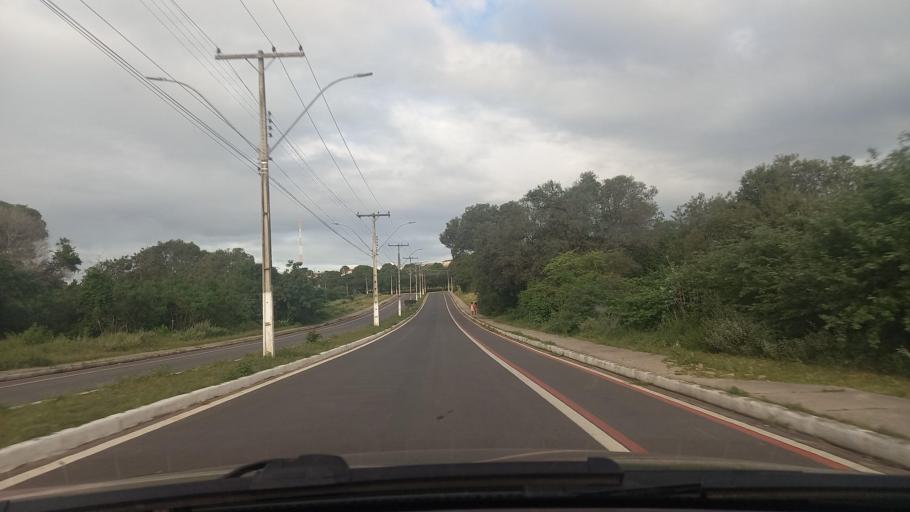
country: BR
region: Sergipe
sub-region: Caninde De Sao Francisco
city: Caninde de Sao Francisco
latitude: -9.6061
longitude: -37.7687
